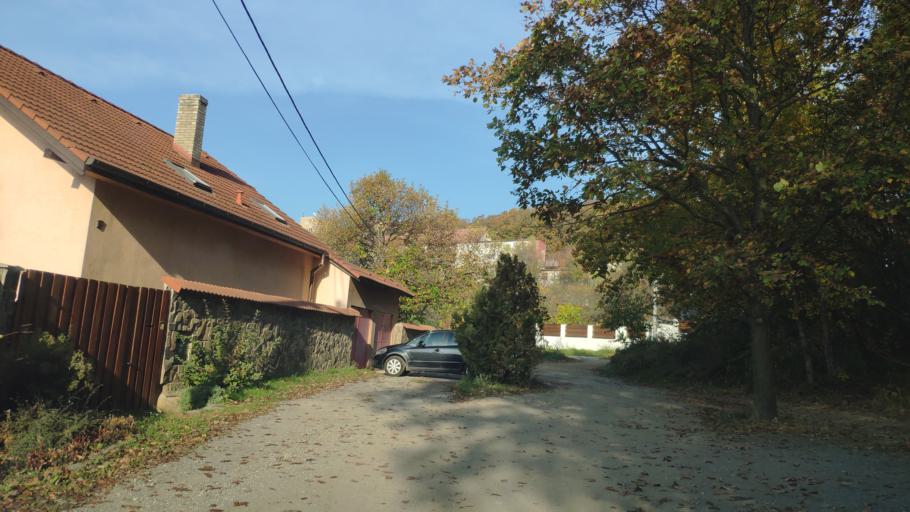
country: SK
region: Kosicky
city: Kosice
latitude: 48.7439
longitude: 21.2149
